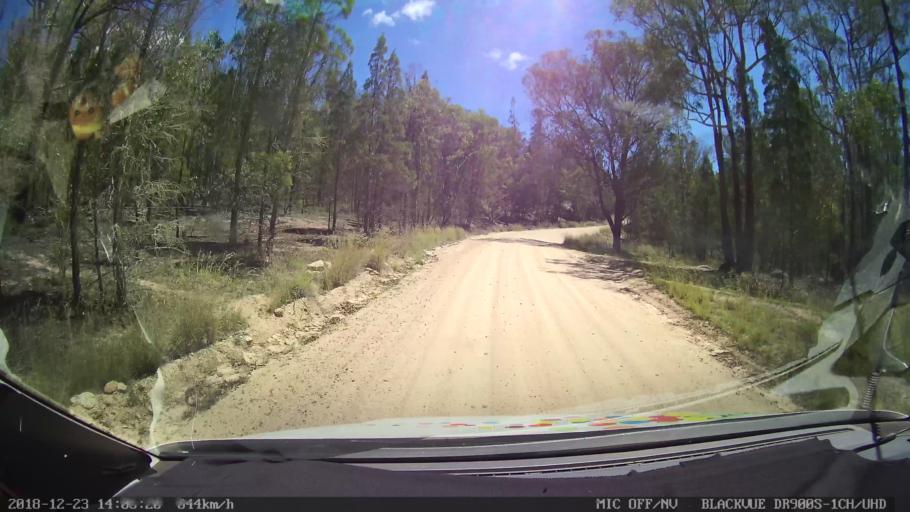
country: AU
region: New South Wales
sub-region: Tamworth Municipality
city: Manilla
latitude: -30.6300
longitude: 151.0766
